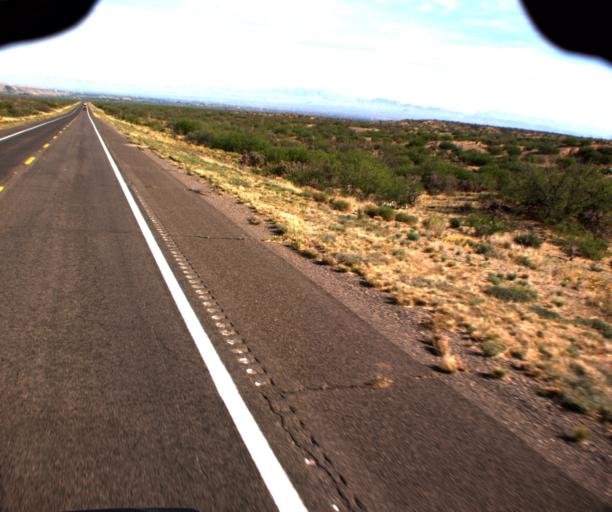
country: US
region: Arizona
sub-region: Graham County
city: Swift Trail Junction
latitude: 32.6306
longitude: -109.6914
